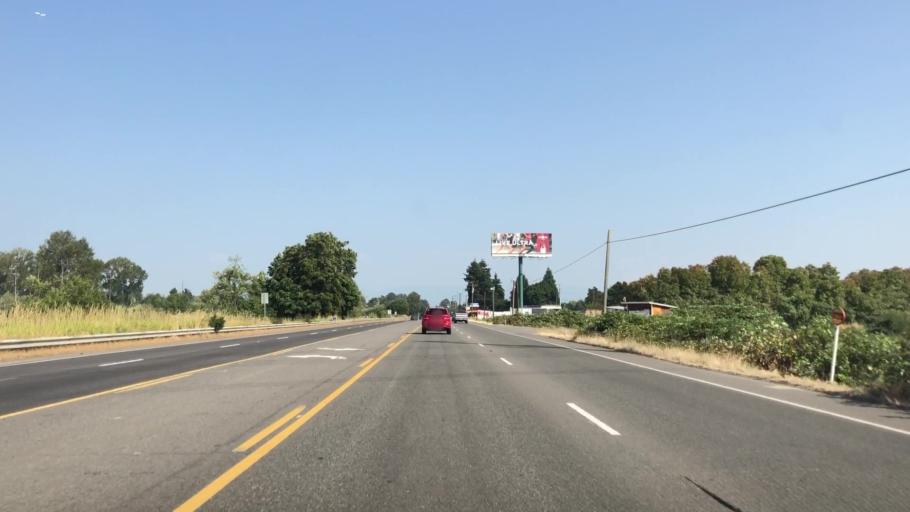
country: US
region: Washington
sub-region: Pierce County
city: Fife
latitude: 47.2264
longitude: -122.3686
